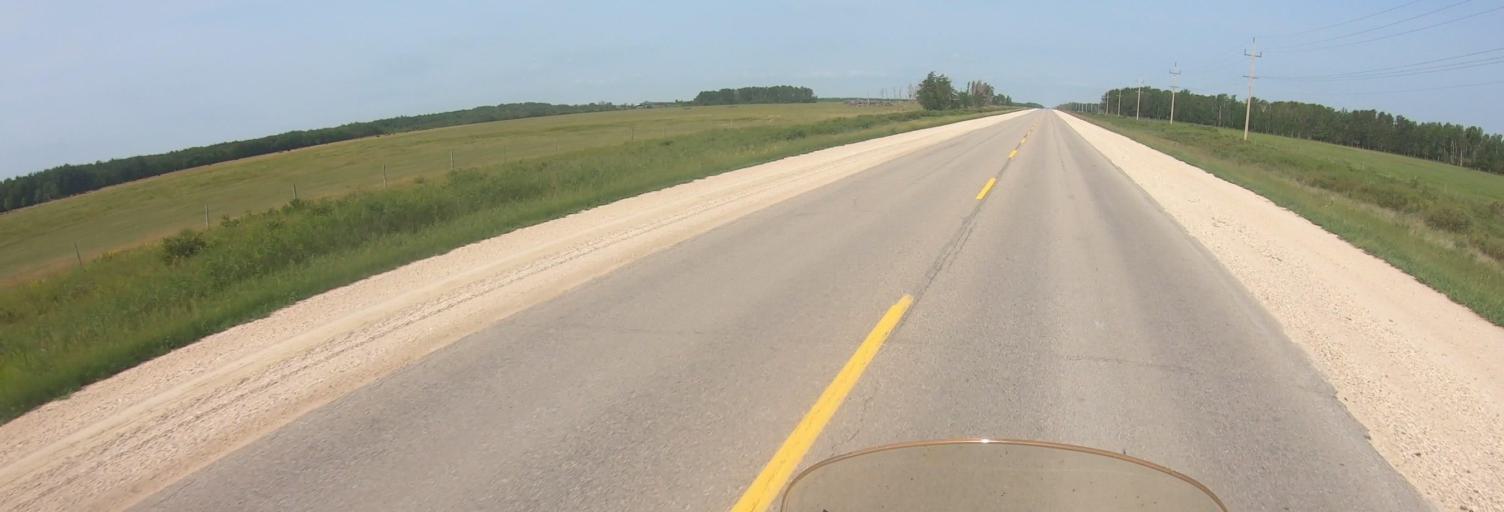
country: CA
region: Manitoba
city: La Broquerie
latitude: 49.3084
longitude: -96.5619
